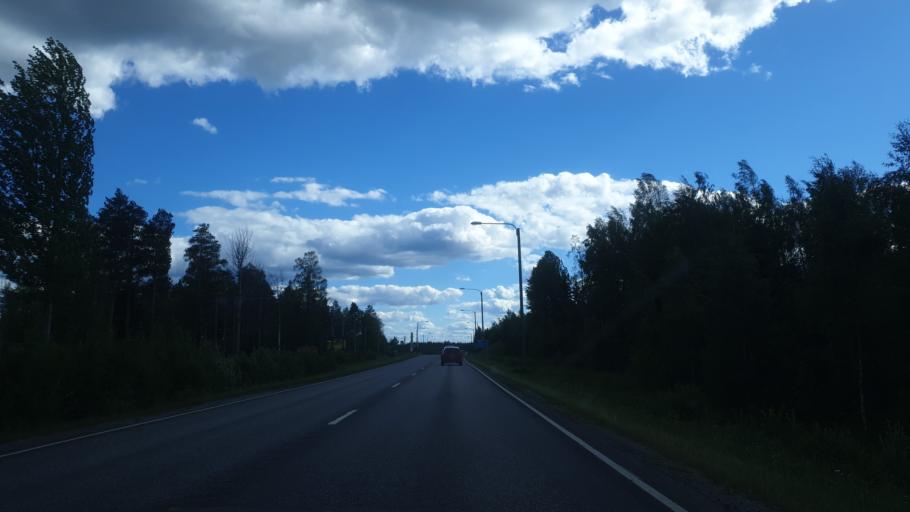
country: FI
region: Southern Savonia
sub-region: Pieksaemaeki
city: Juva
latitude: 61.9056
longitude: 27.8047
